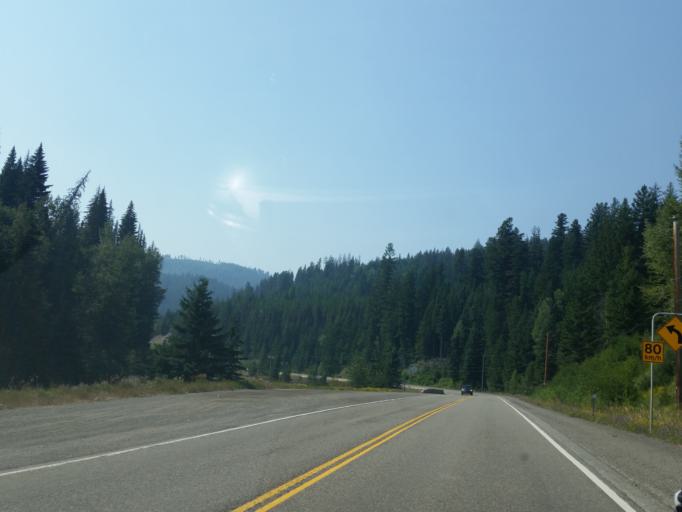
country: CA
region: British Columbia
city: Princeton
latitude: 49.1643
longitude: -120.5827
